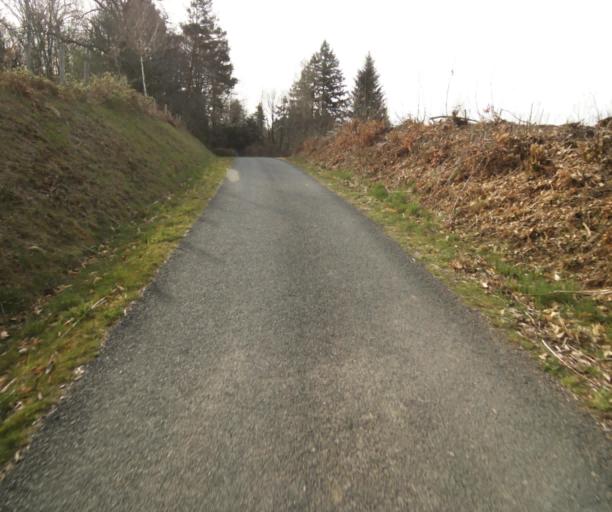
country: FR
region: Limousin
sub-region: Departement de la Correze
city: Chamboulive
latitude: 45.4371
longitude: 1.7594
